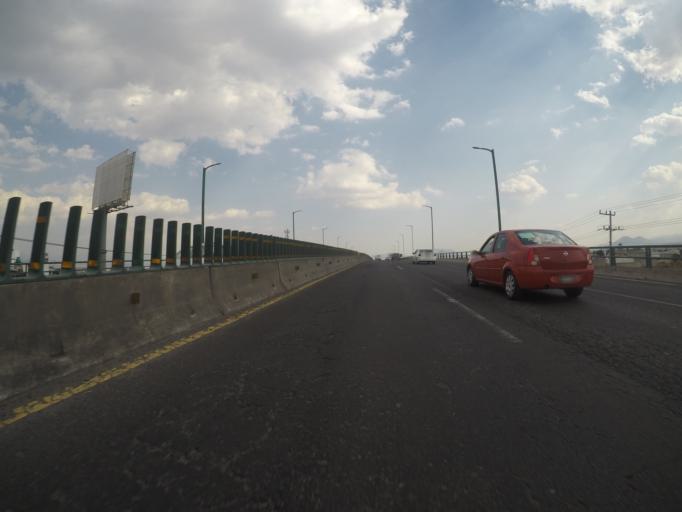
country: MX
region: Morelos
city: San Miguel Totocuitlapilco
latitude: 19.2366
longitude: -99.5983
